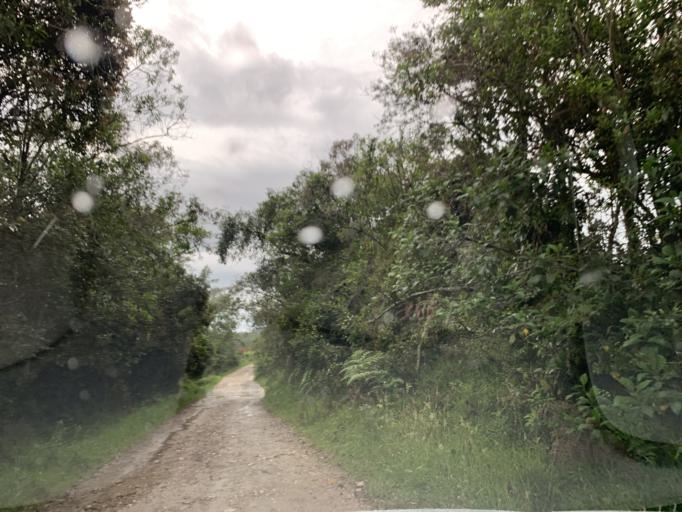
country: CO
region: Boyaca
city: Arcabuco
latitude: 5.7571
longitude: -73.4775
